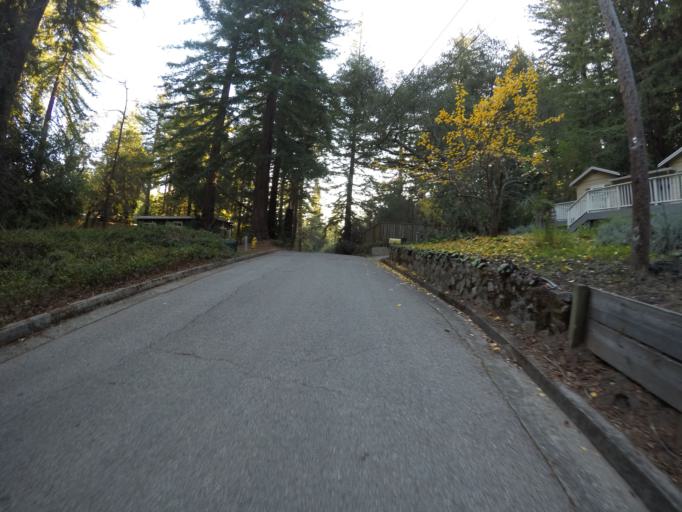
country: US
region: California
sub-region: Santa Cruz County
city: Scotts Valley
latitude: 37.0775
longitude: -121.9928
